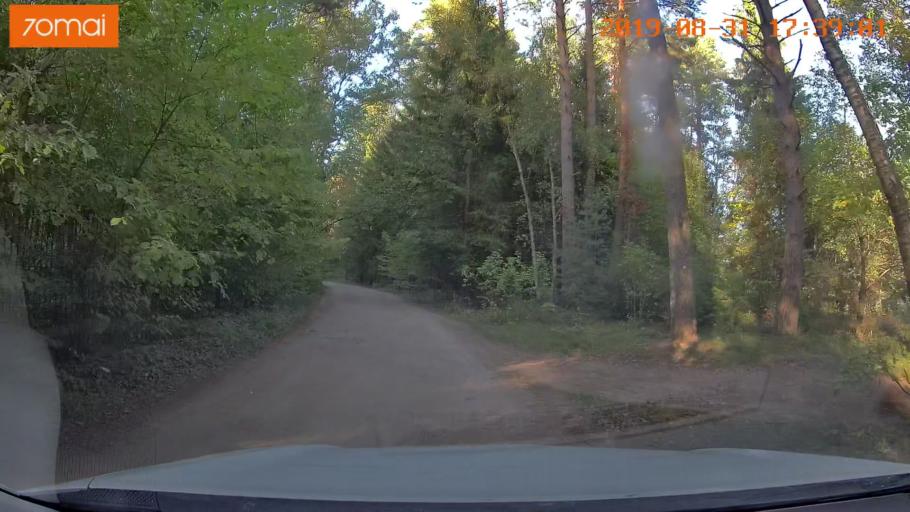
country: RU
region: Kaluga
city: Detchino
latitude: 54.8164
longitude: 36.3620
